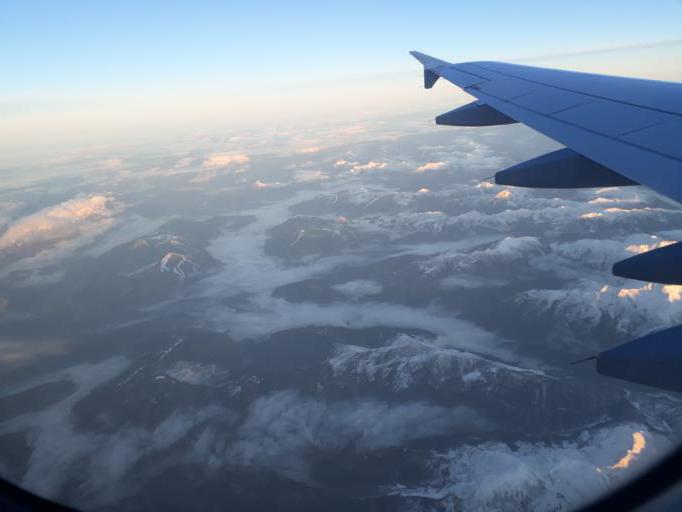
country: AT
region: Tyrol
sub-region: Politischer Bezirk Kufstein
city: Alpbach
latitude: 47.3680
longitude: 11.9270
